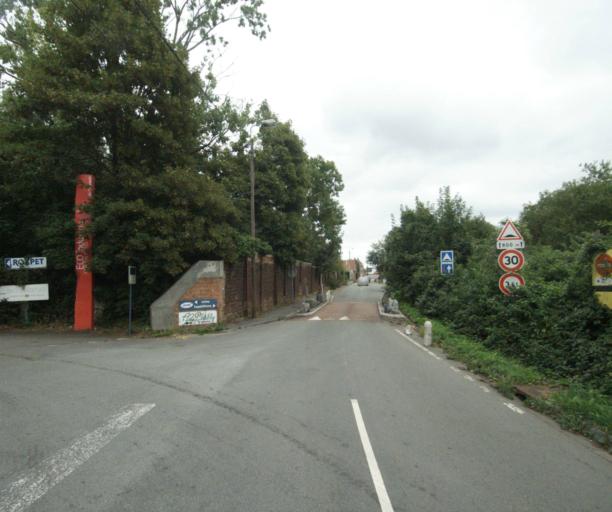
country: FR
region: Nord-Pas-de-Calais
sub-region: Departement du Nord
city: Lesquin
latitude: 50.5850
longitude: 3.1236
